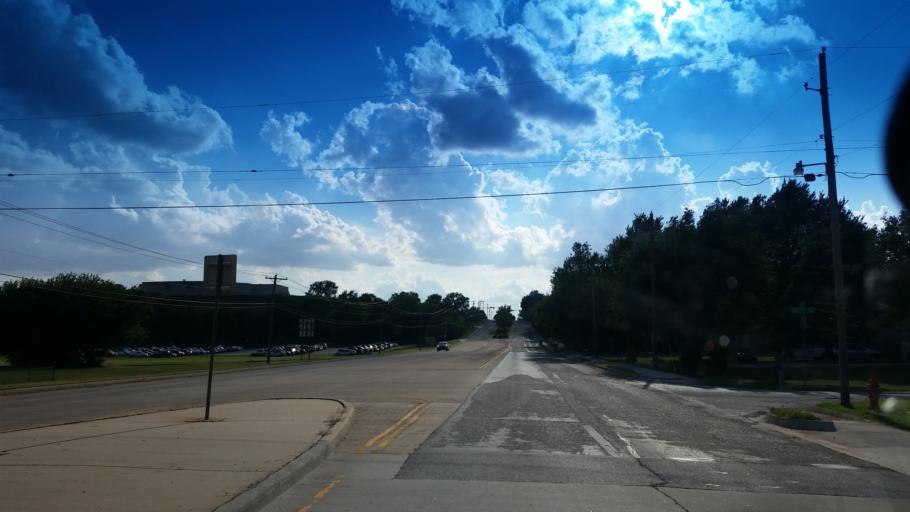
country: US
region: Oklahoma
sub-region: Oklahoma County
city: Nichols Hills
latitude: 35.5368
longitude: -97.4784
